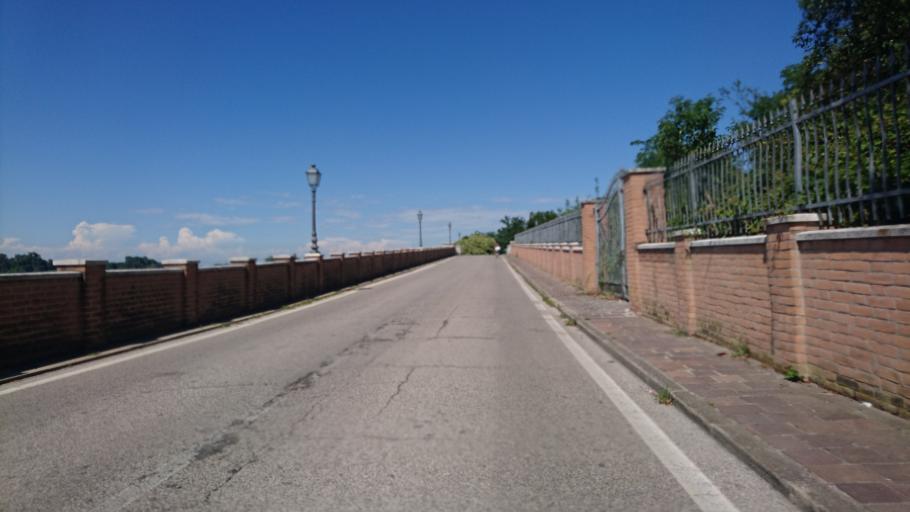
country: IT
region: Veneto
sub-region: Provincia di Venezia
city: Lido
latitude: 45.4268
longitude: 12.3793
